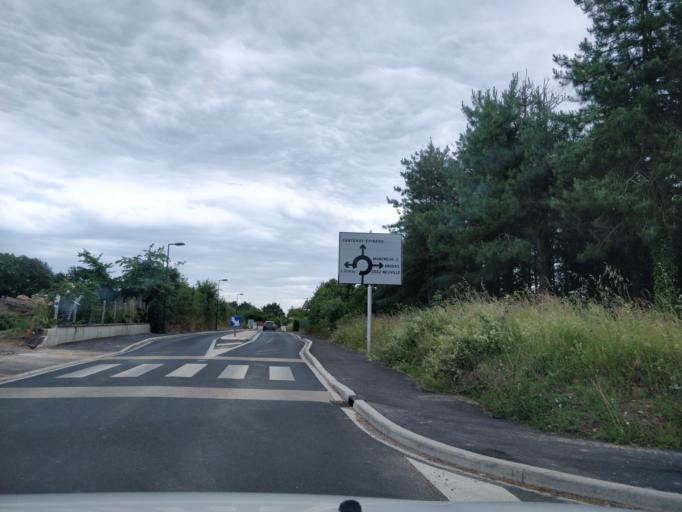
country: FR
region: Pays de la Loire
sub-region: Departement de Maine-et-Loire
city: Feneu
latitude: 47.5678
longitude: -0.5883
